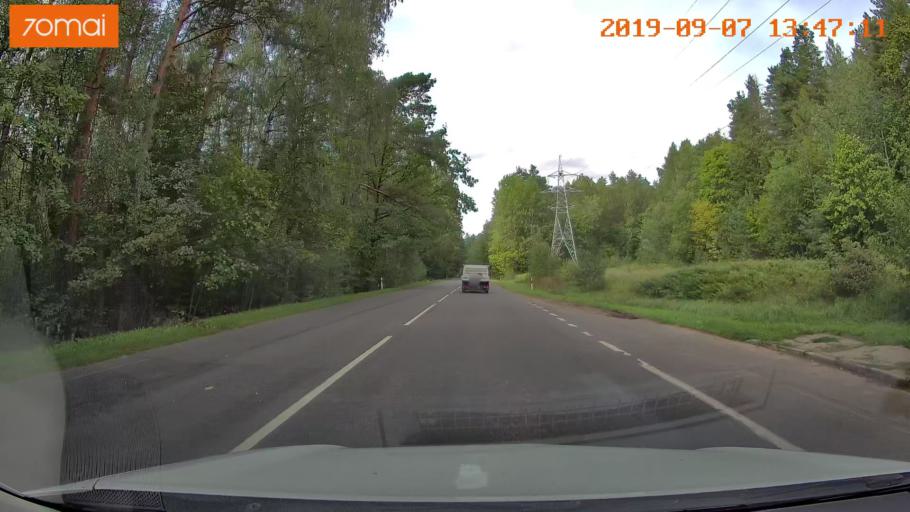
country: LT
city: Baltoji Voke
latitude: 54.5953
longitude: 25.2177
